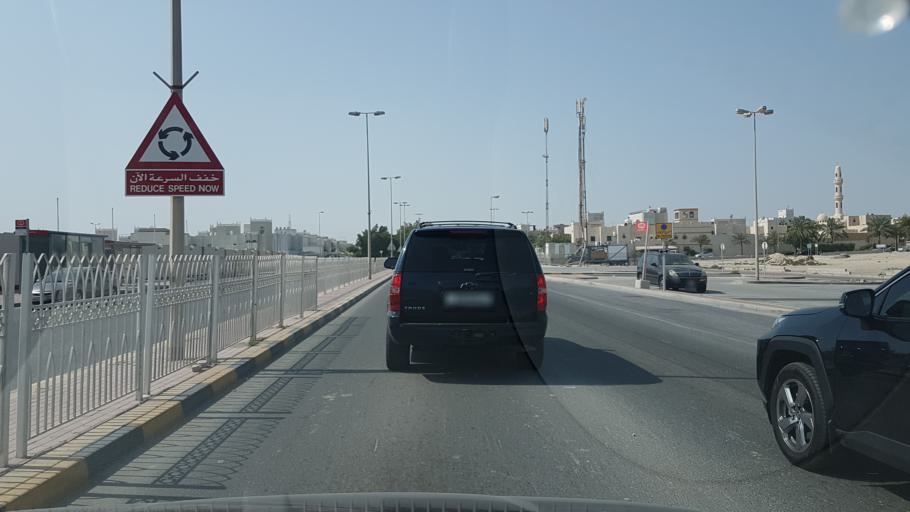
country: BH
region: Northern
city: Madinat `Isa
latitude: 26.1688
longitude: 50.5409
